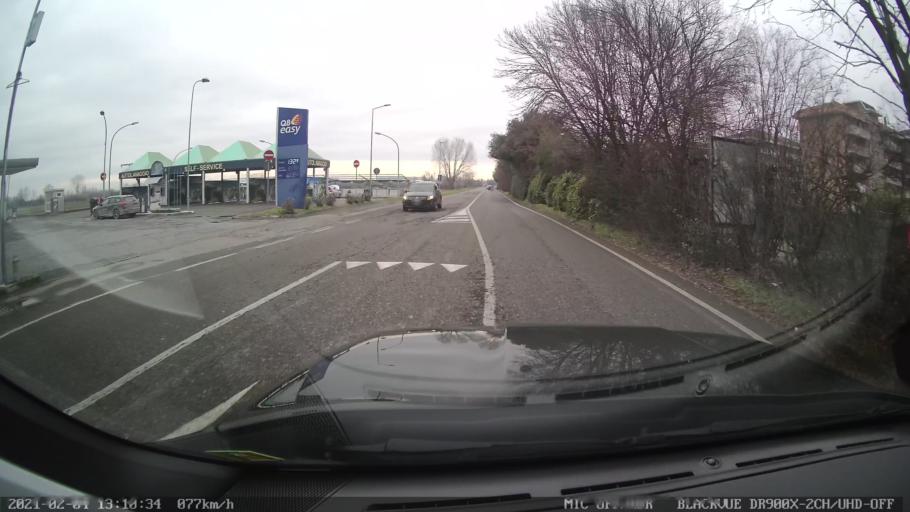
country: IT
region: Piedmont
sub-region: Provincia di Novara
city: Novara
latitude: 45.4643
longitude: 8.6102
